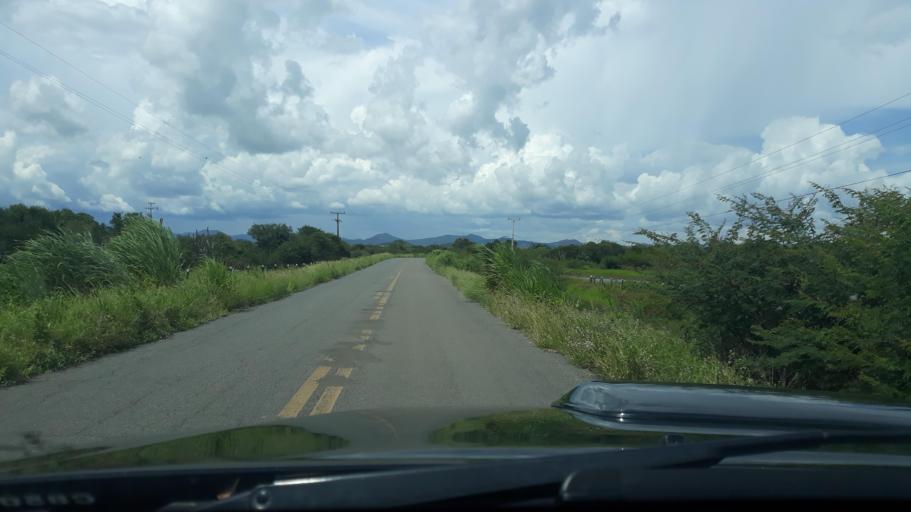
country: BR
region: Bahia
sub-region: Guanambi
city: Guanambi
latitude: -14.0242
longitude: -42.8681
